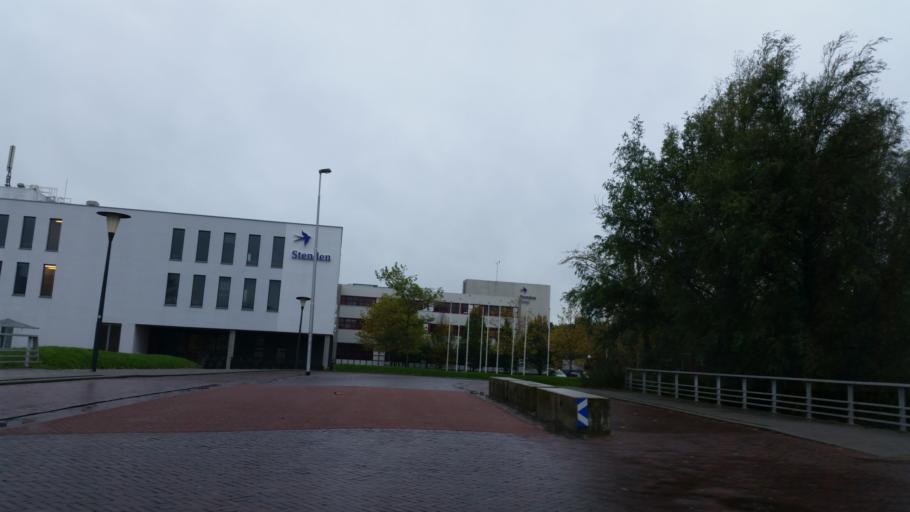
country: NL
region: Friesland
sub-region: Gemeente Leeuwarden
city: Bilgaard
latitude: 53.2115
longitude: 5.7967
